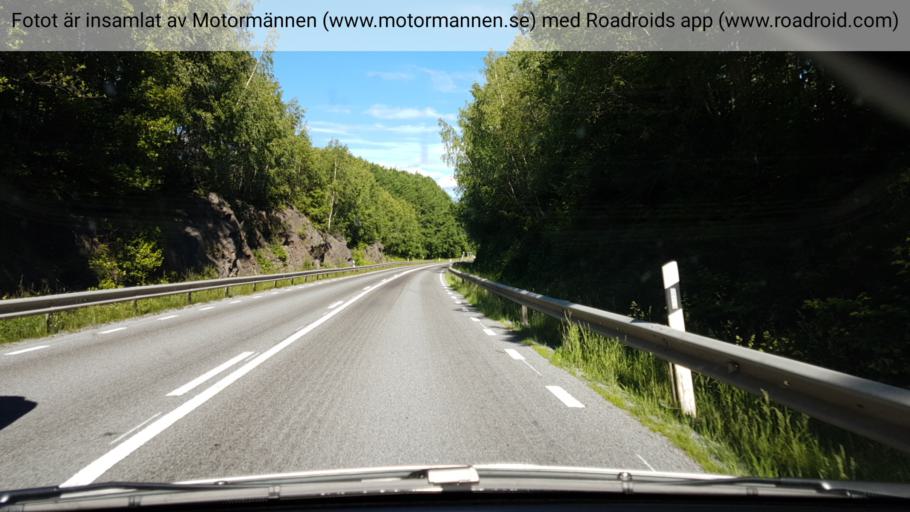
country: SE
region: Vaestra Goetaland
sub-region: Toreboda Kommun
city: Toereboda
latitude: 58.7085
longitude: 13.9960
